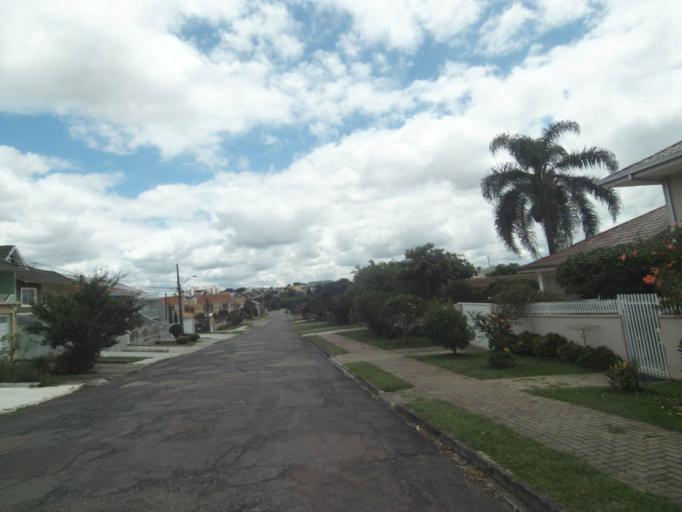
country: BR
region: Parana
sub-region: Curitiba
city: Curitiba
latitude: -25.4883
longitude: -49.2782
